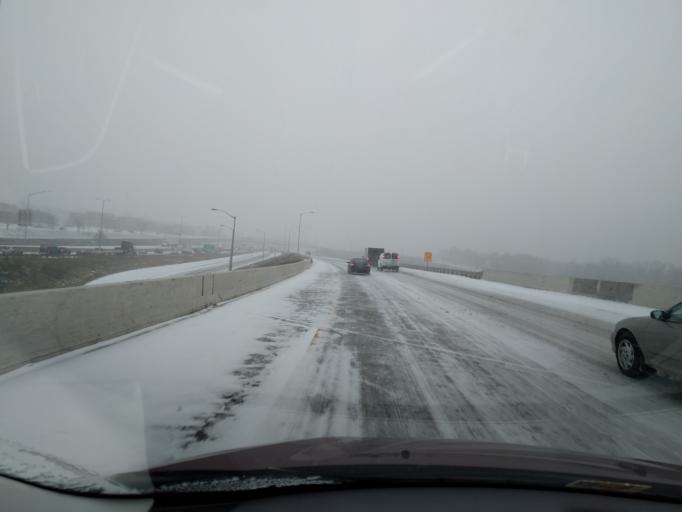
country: US
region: Wisconsin
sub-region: Waukesha County
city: Butler
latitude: 43.1586
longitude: -88.0630
